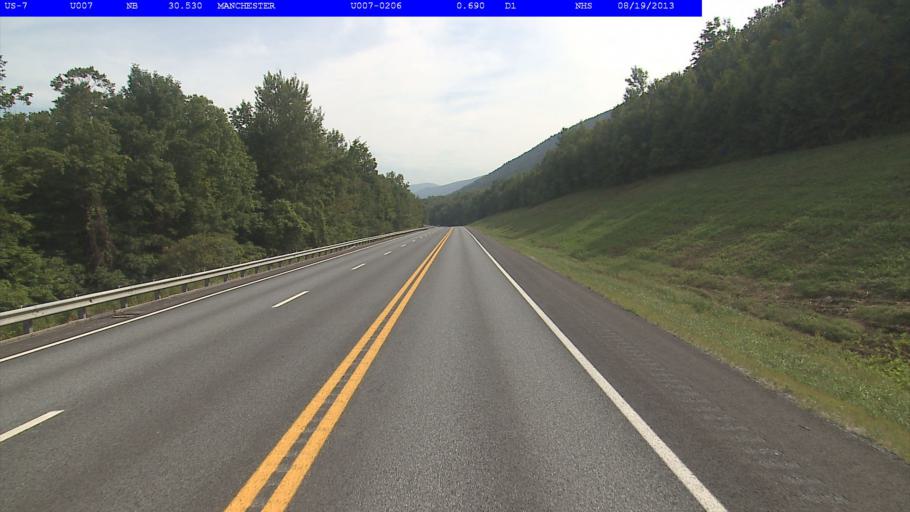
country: US
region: Vermont
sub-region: Bennington County
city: Manchester Center
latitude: 43.1255
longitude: -73.0716
